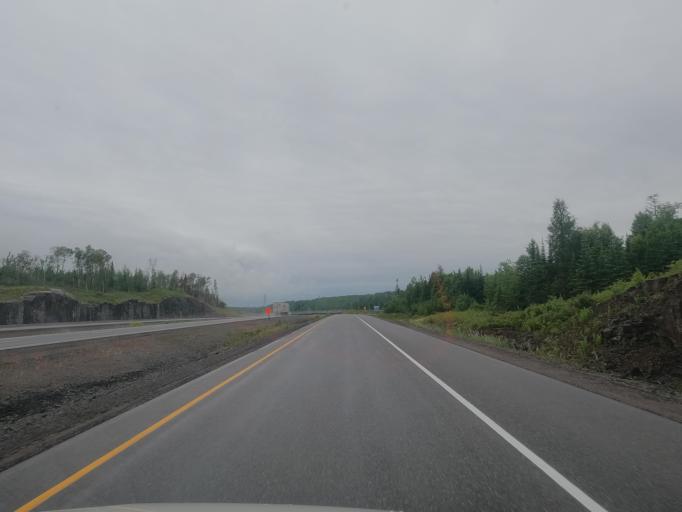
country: CA
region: Ontario
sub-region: Thunder Bay District
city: Thunder Bay
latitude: 48.4840
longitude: -89.1751
